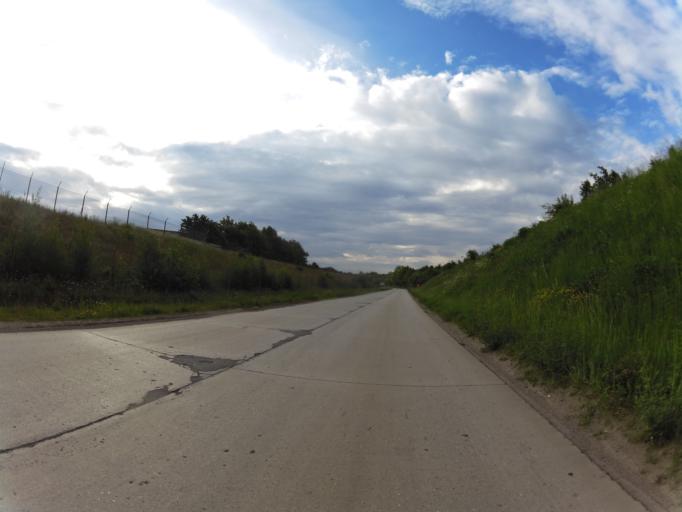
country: NL
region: Limburg
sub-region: Gemeente Brunssum
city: Brunssum
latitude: 50.9444
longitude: 5.9989
